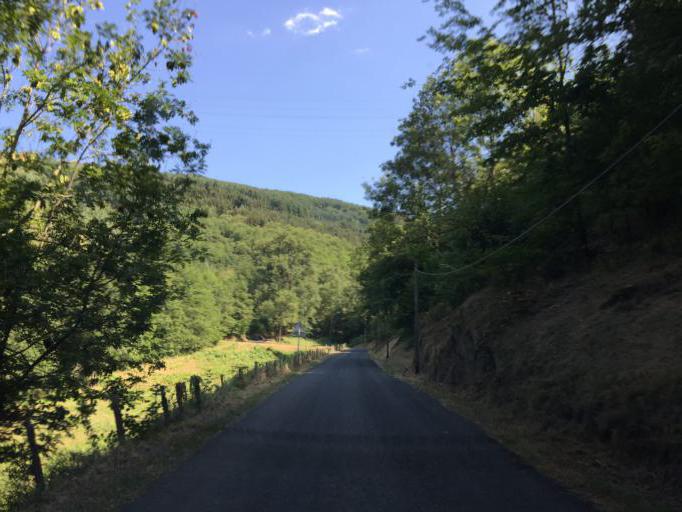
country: FR
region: Rhone-Alpes
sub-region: Departement de la Loire
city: Saint-Jean-Bonnefonds
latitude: 45.4311
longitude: 4.4567
